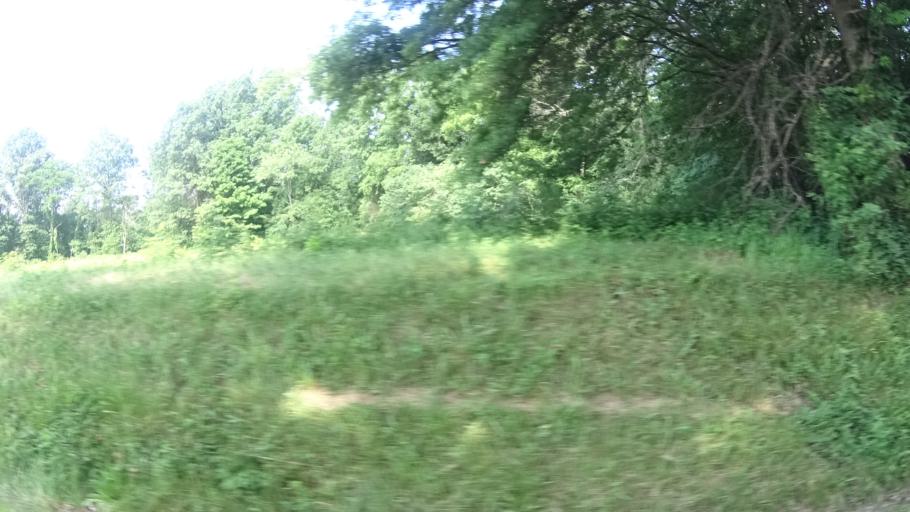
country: US
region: Ohio
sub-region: Lorain County
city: Vermilion
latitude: 41.3842
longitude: -82.4302
